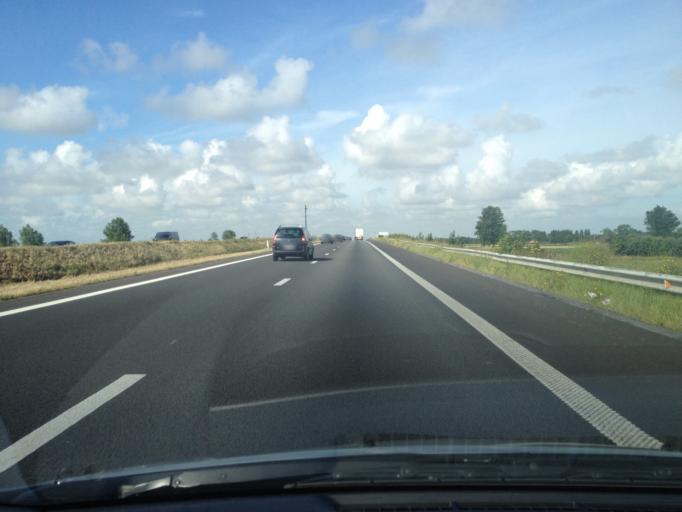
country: BE
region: Flanders
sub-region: Provincie West-Vlaanderen
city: Nieuwpoort
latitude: 51.1304
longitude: 2.8040
